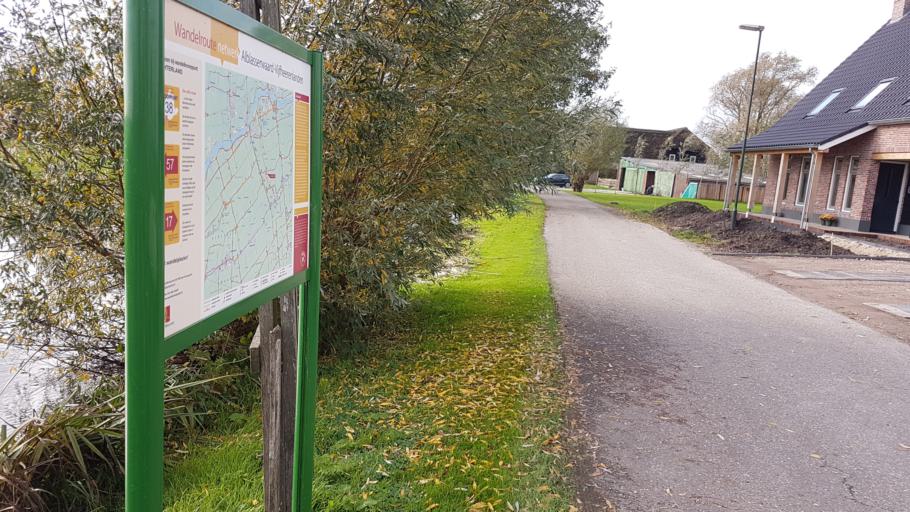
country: NL
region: South Holland
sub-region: Molenwaard
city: Liesveld
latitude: 51.9064
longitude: 4.8489
